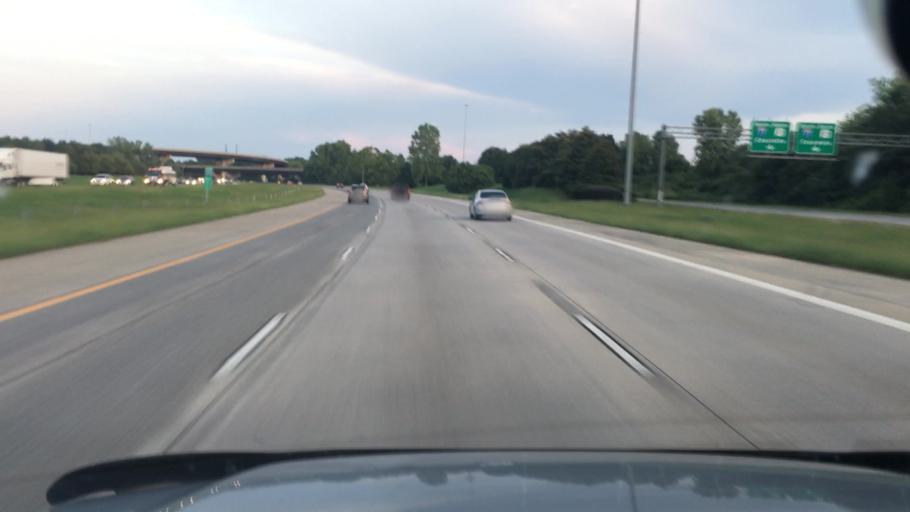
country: US
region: North Carolina
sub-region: Mecklenburg County
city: Pineville
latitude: 35.1290
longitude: -80.9219
